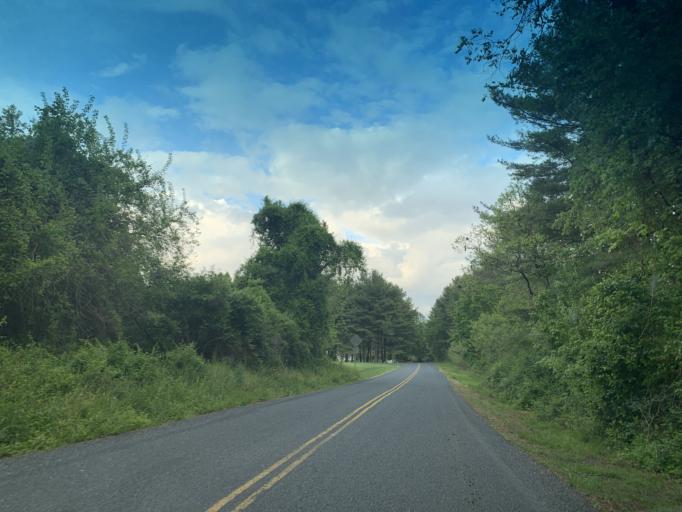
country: US
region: Pennsylvania
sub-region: York County
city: Susquehanna Trails
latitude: 39.6868
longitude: -76.2913
